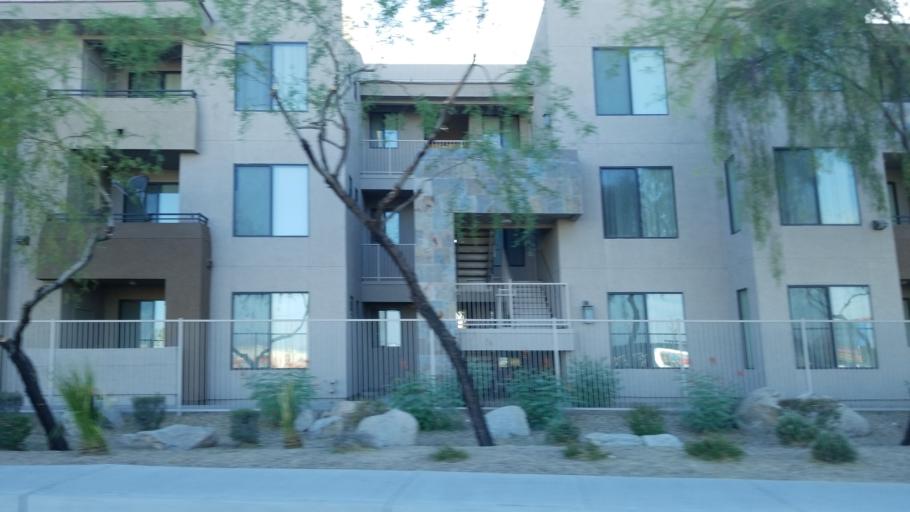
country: US
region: Arizona
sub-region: Maricopa County
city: Paradise Valley
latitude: 33.6690
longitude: -112.0309
